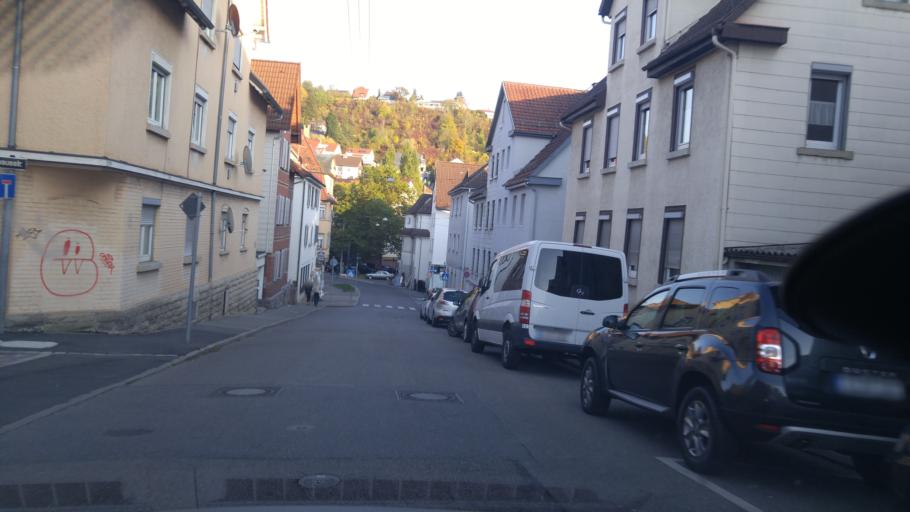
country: DE
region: Baden-Wuerttemberg
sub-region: Regierungsbezirk Stuttgart
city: Stuttgart Feuerbach
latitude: 48.8059
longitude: 9.1574
